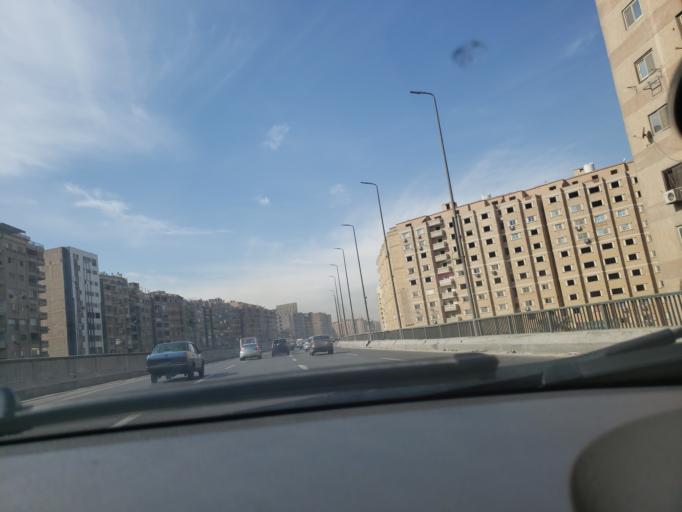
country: EG
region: Al Jizah
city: Al Jizah
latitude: 29.9759
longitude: 31.1674
